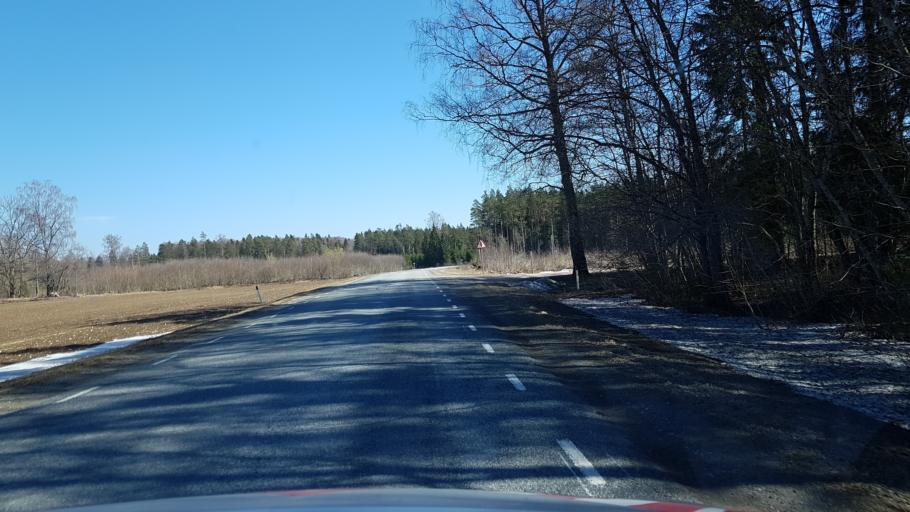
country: EE
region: Laeaene-Virumaa
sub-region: Vaeike-Maarja vald
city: Vaike-Maarja
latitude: 59.1238
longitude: 26.3035
